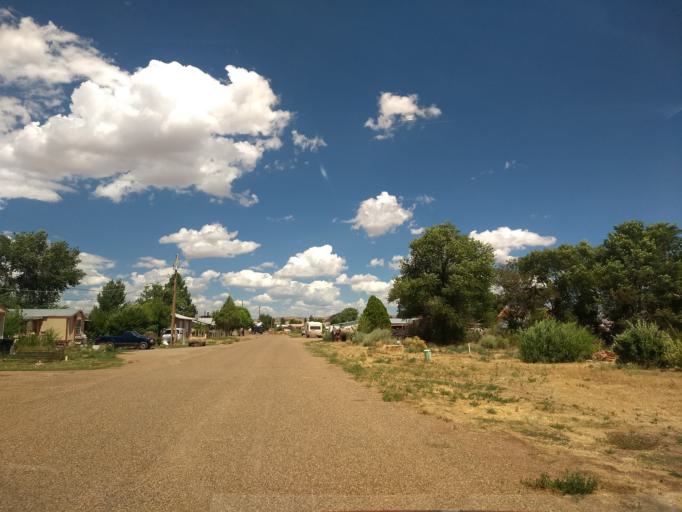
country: US
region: Arizona
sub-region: Coconino County
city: Fredonia
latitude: 36.9459
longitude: -112.5188
